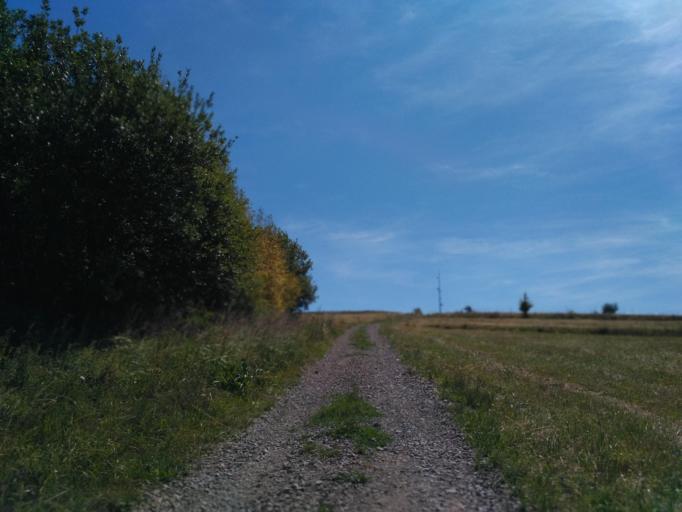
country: PL
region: Subcarpathian Voivodeship
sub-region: Powiat sanocki
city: Bukowsko
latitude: 49.4885
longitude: 22.0744
